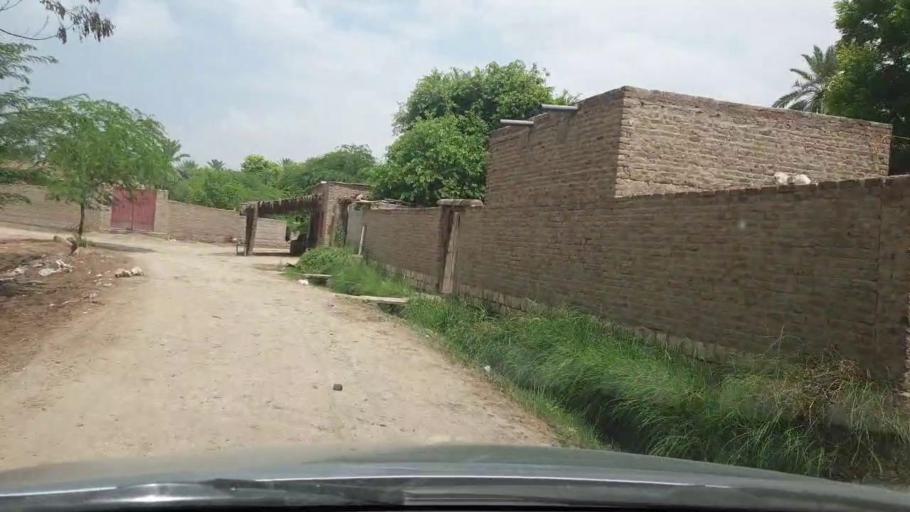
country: PK
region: Sindh
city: Kot Diji
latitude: 27.4188
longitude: 68.7628
